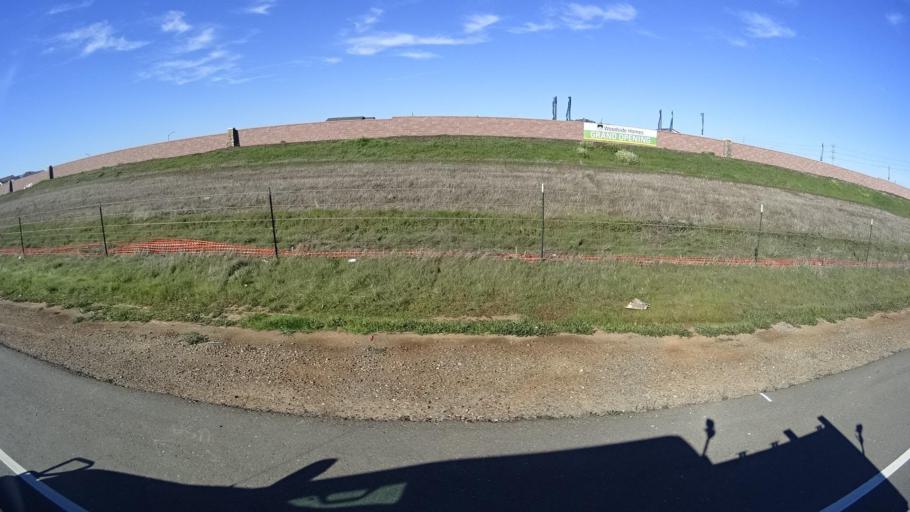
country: US
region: California
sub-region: Sacramento County
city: Gold River
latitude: 38.5566
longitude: -121.1888
